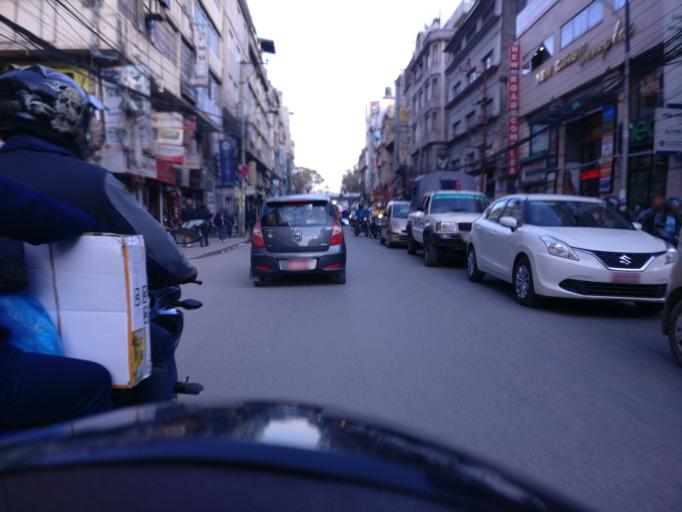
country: NP
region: Central Region
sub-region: Bagmati Zone
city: Kathmandu
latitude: 27.7034
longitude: 85.3116
